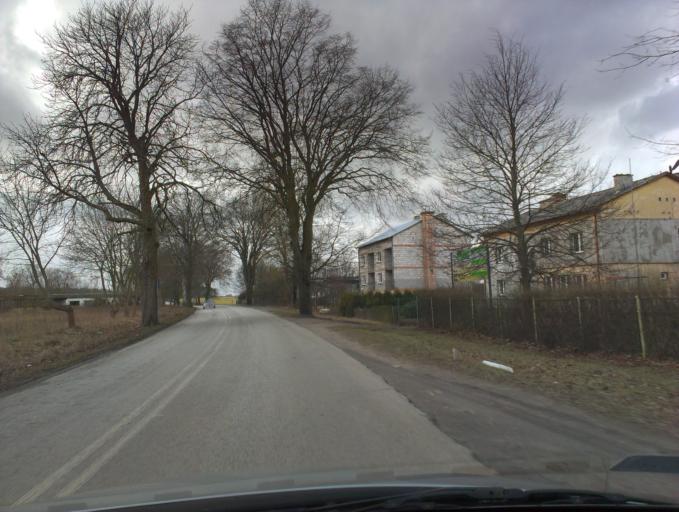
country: PL
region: Pomeranian Voivodeship
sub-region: Powiat czluchowski
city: Rzeczenica
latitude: 53.6896
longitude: 17.0390
